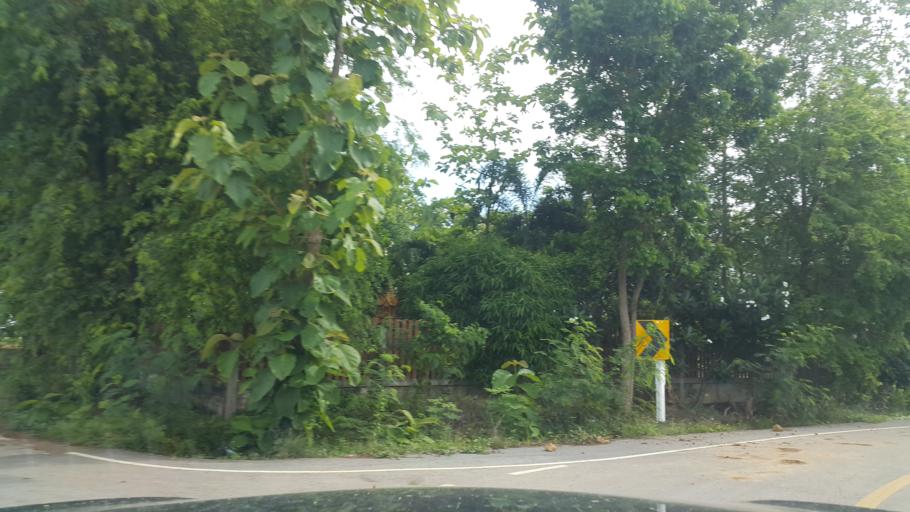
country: TH
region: Sukhothai
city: Si Nakhon
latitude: 17.2686
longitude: 99.9329
